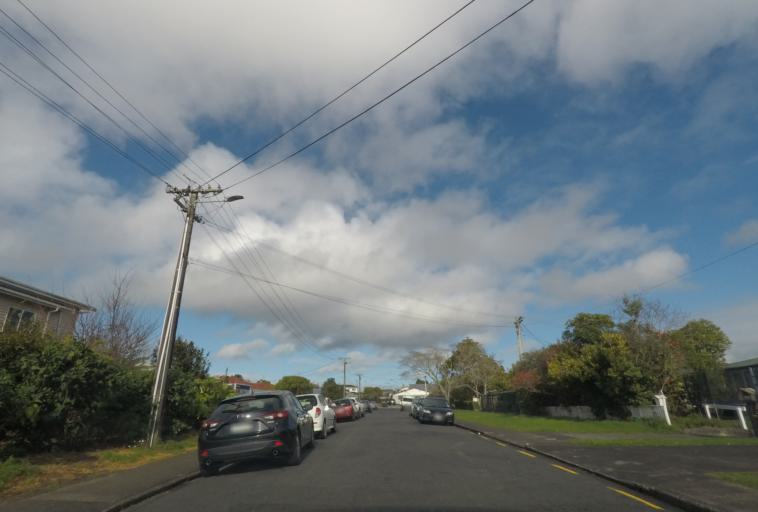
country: NZ
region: Auckland
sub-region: Auckland
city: Waitakere
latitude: -36.9007
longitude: 174.6649
